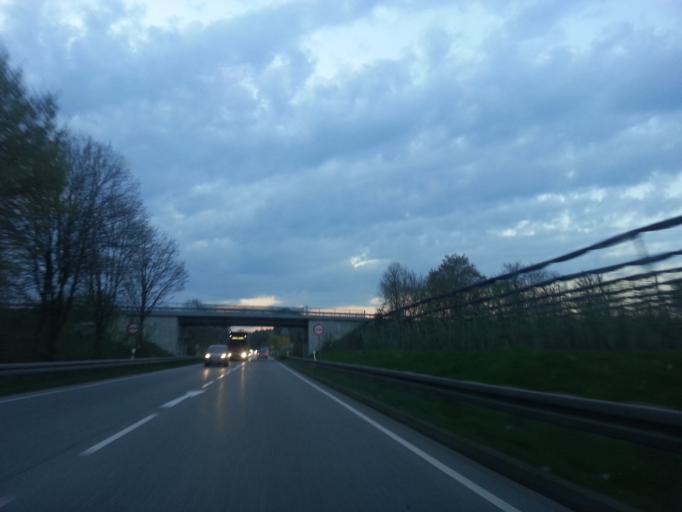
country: DE
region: Baden-Wuerttemberg
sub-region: Tuebingen Region
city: Eriskirch
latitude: 47.6138
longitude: 9.5697
